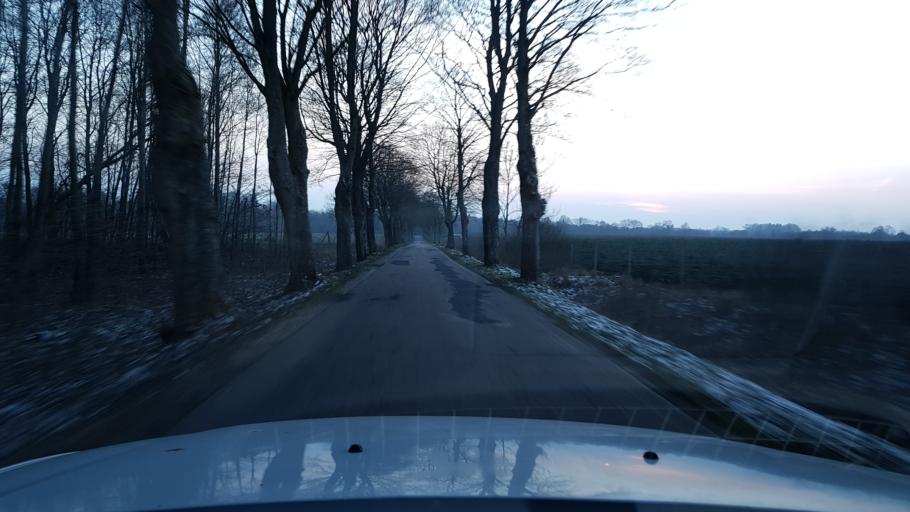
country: PL
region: West Pomeranian Voivodeship
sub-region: Powiat bialogardzki
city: Karlino
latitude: 54.0142
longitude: 15.8445
